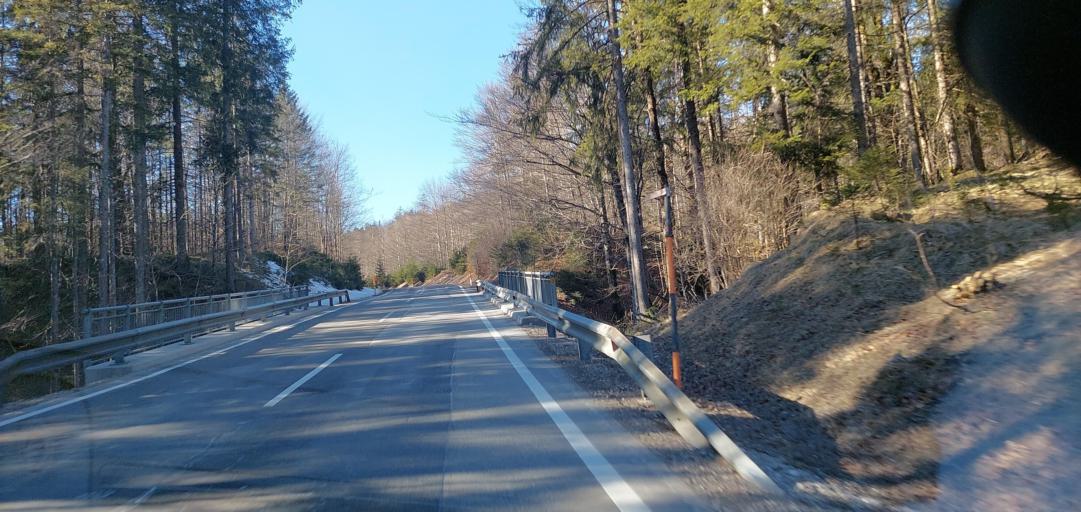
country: AT
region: Upper Austria
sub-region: Politischer Bezirk Gmunden
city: Bad Ischl
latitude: 47.7690
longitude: 13.6312
